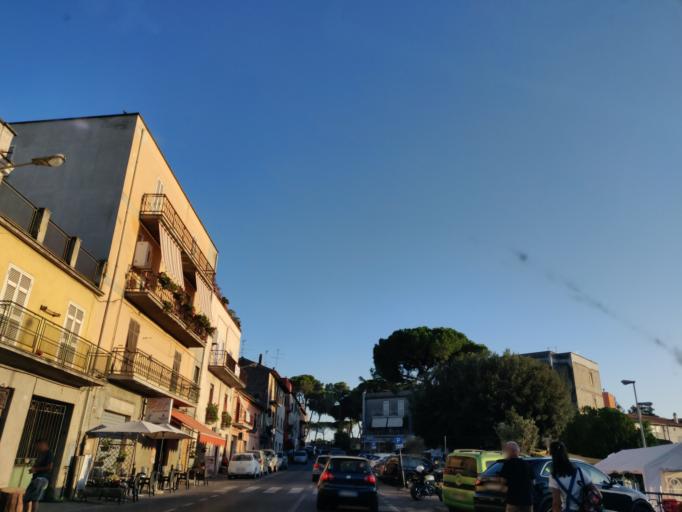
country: IT
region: Latium
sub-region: Provincia di Viterbo
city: Canino
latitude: 42.4636
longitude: 11.7493
